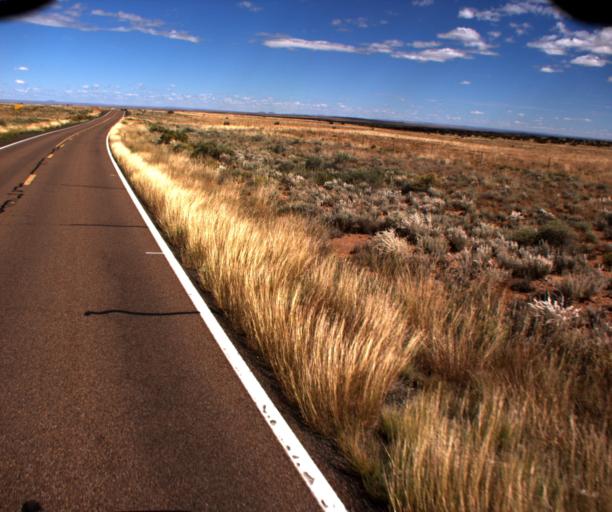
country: US
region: Arizona
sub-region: Navajo County
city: Holbrook
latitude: 34.7230
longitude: -110.2920
